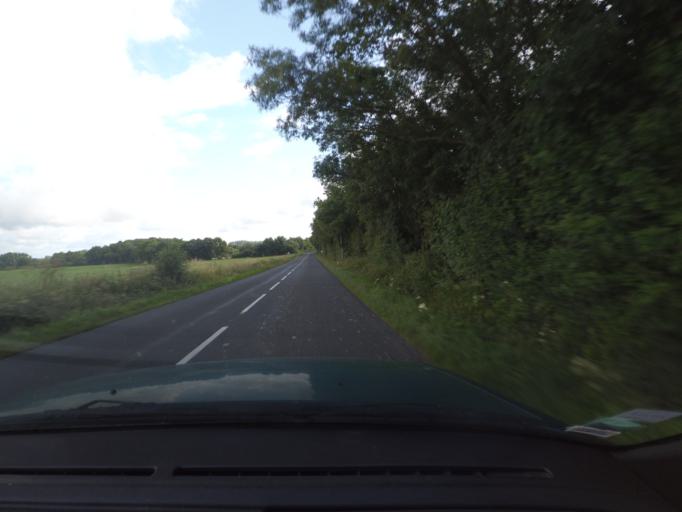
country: FR
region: Pays de la Loire
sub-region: Departement de la Vendee
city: Saint-Hilaire-de-Loulay
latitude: 47.0294
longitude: -1.3293
